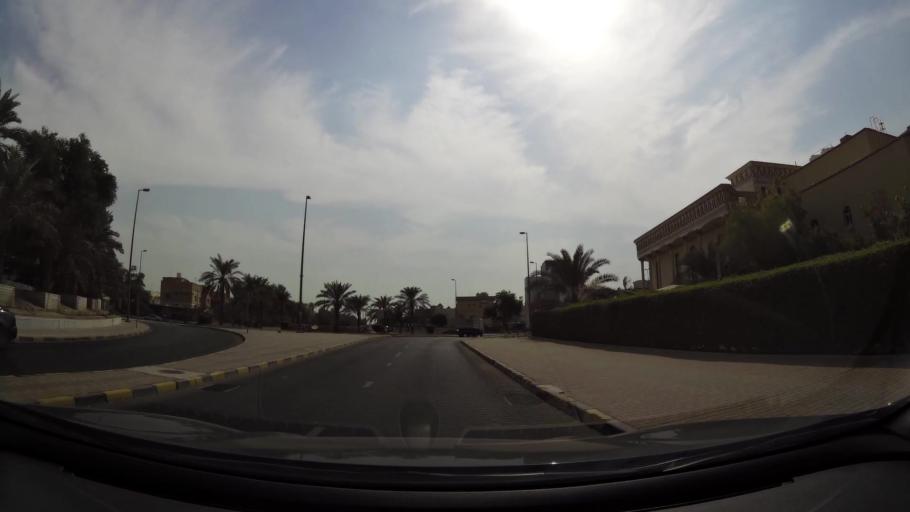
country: KW
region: Al Asimah
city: Ash Shamiyah
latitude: 29.3496
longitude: 47.9678
